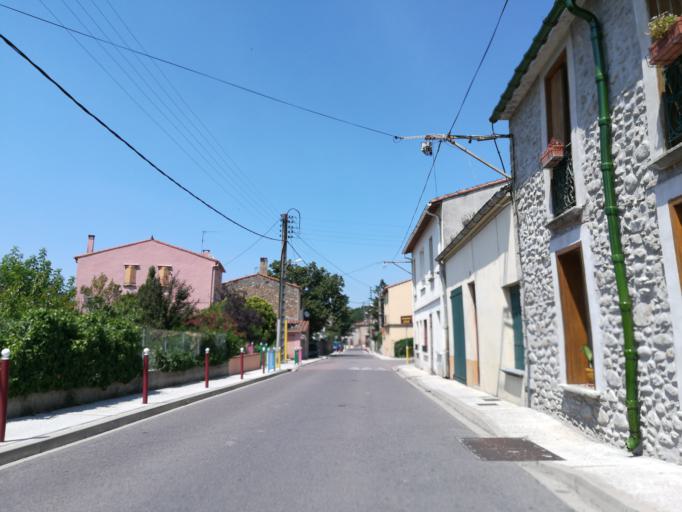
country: FR
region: Languedoc-Roussillon
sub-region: Departement des Pyrenees-Orientales
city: Maureillas-las-Illas
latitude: 42.4900
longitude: 2.8094
